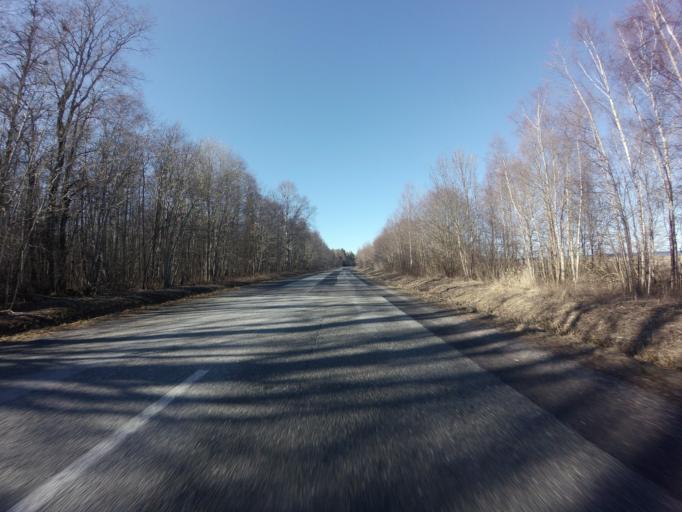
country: EE
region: Saare
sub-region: Kuressaare linn
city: Kuressaare
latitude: 58.5823
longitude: 22.6227
